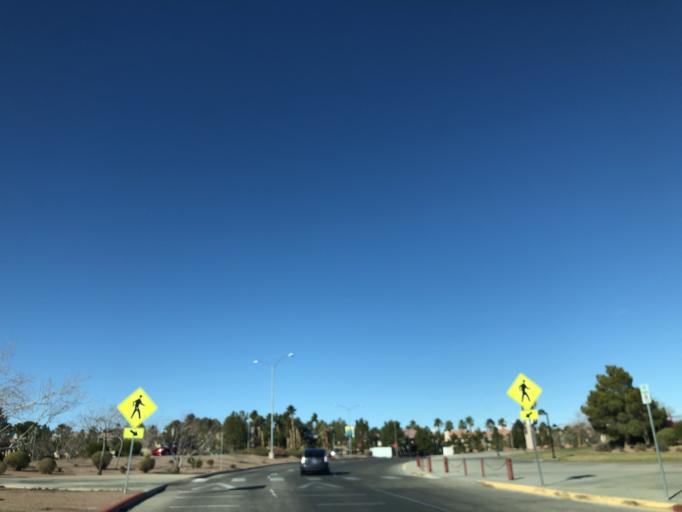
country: US
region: Nevada
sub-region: Clark County
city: Whitney
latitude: 36.0184
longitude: -115.0814
